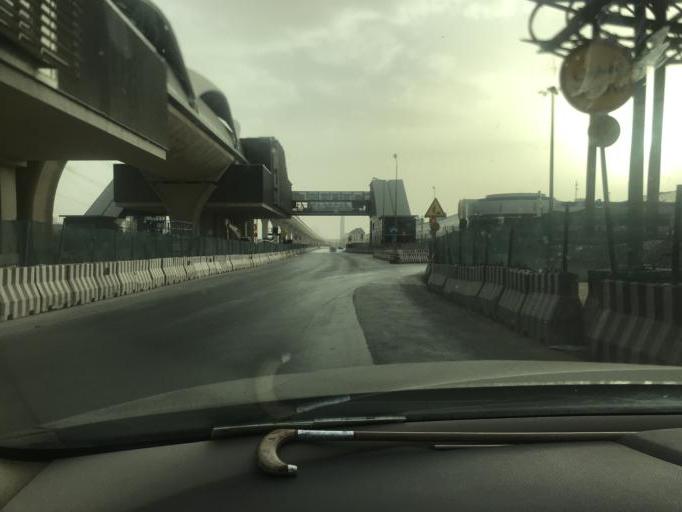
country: SA
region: Ar Riyad
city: Riyadh
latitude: 24.7868
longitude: 46.6608
